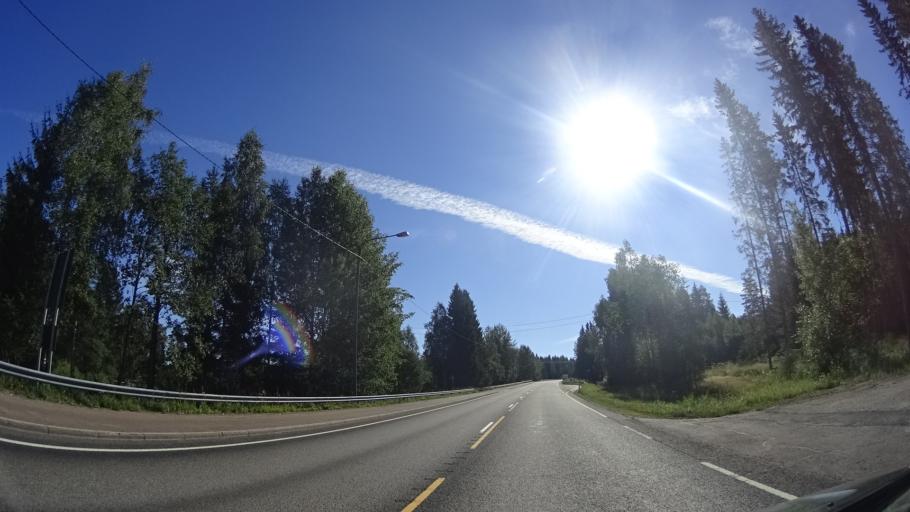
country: FI
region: Central Finland
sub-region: Jyvaeskylae
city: Petaejaevesi
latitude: 62.2715
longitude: 25.3183
